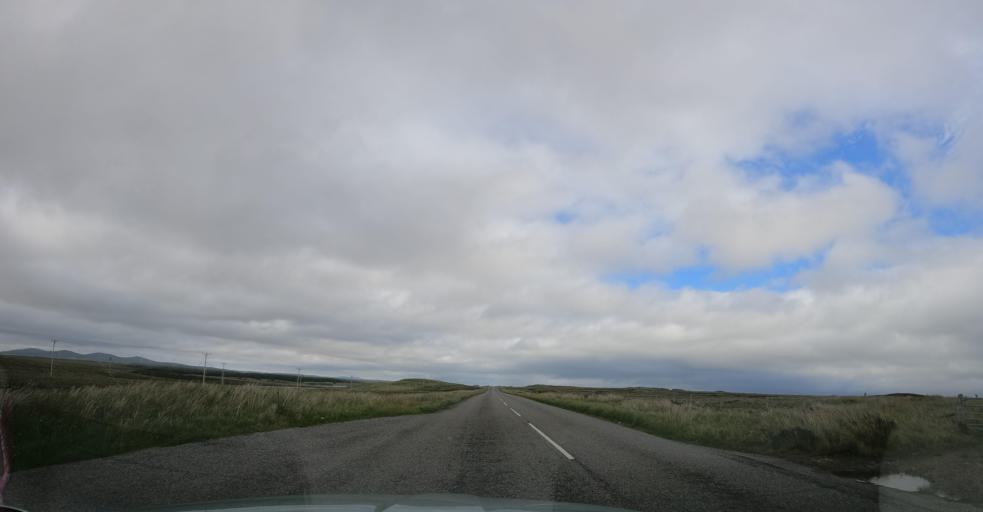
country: GB
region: Scotland
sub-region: Eilean Siar
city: Stornoway
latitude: 58.1637
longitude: -6.4904
